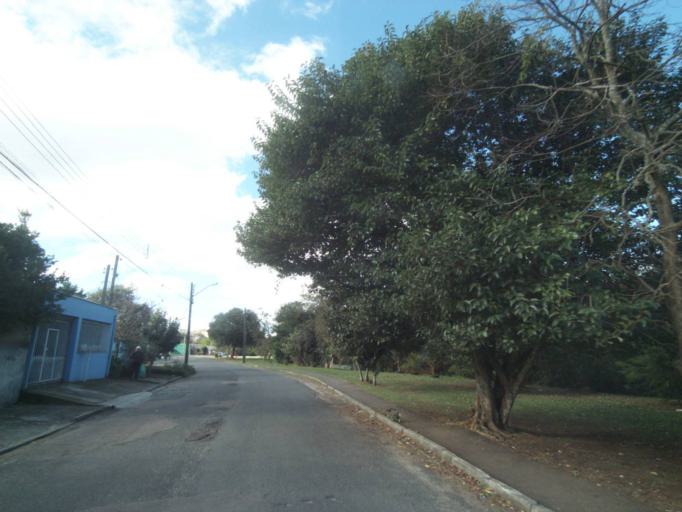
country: BR
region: Parana
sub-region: Sao Jose Dos Pinhais
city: Sao Jose dos Pinhais
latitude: -25.5327
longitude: -49.2809
